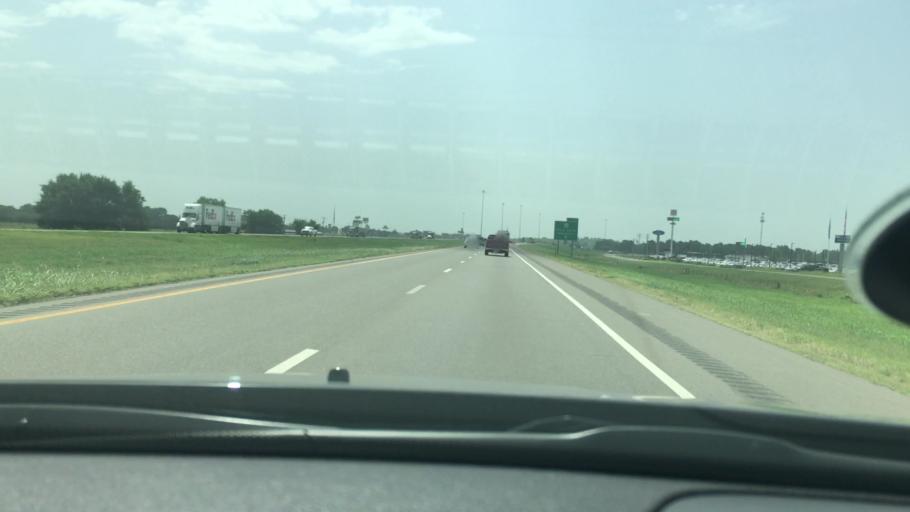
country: US
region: Oklahoma
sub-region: Garvin County
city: Pauls Valley
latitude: 34.7462
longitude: -97.2702
